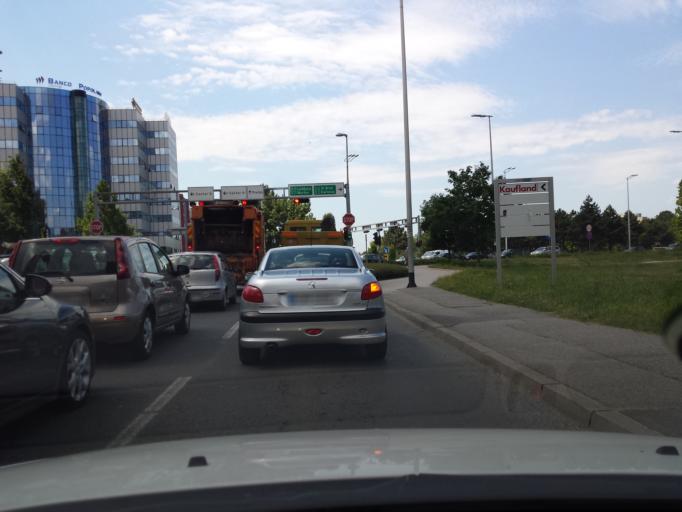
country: HR
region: Grad Zagreb
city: Jankomir
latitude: 45.7967
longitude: 15.9091
